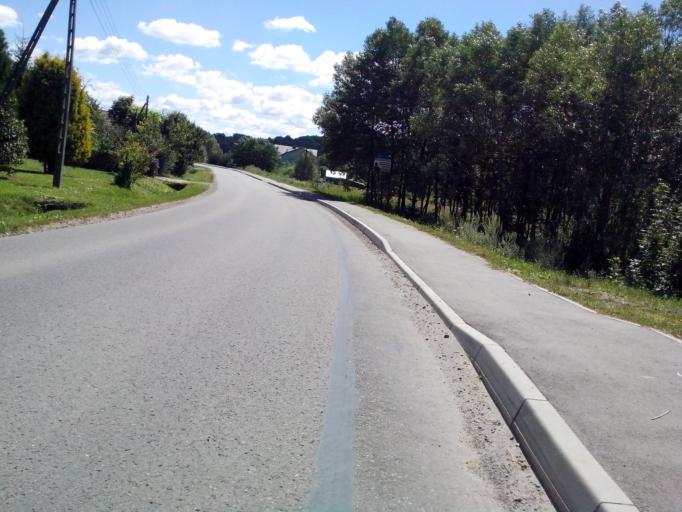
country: PL
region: Subcarpathian Voivodeship
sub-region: Powiat brzozowski
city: Domaradz
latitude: 49.7923
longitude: 21.9529
